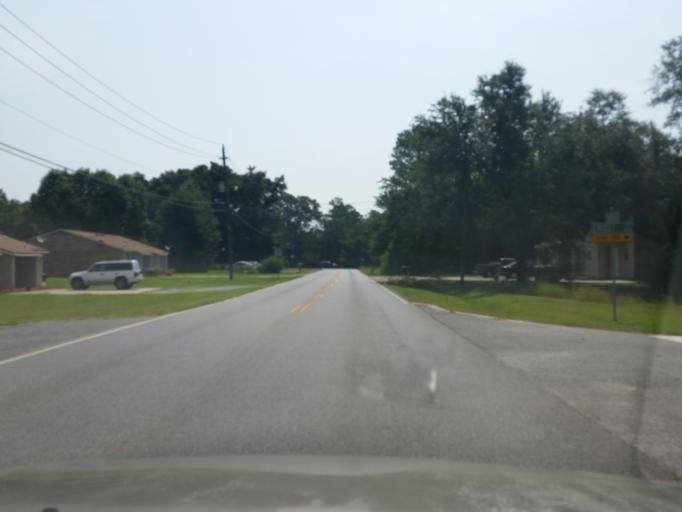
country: US
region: Florida
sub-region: Escambia County
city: Ferry Pass
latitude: 30.5173
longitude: -87.2395
